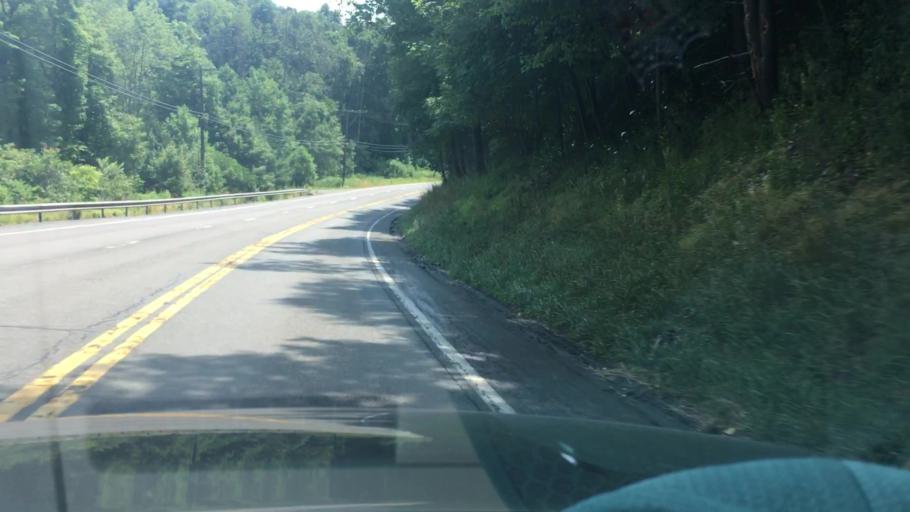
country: US
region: Pennsylvania
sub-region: Schuylkill County
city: Coaldale
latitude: 40.7466
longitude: -75.8976
